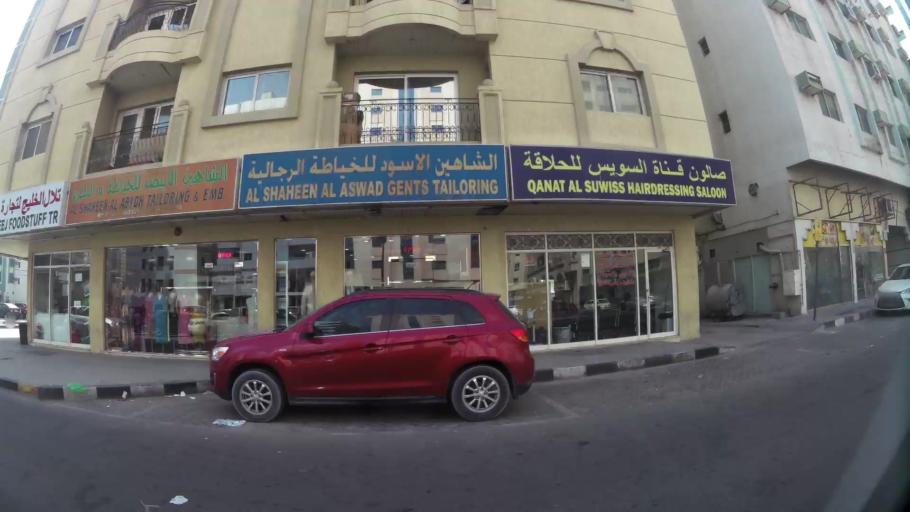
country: AE
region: Ash Shariqah
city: Sharjah
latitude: 25.3484
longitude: 55.3935
